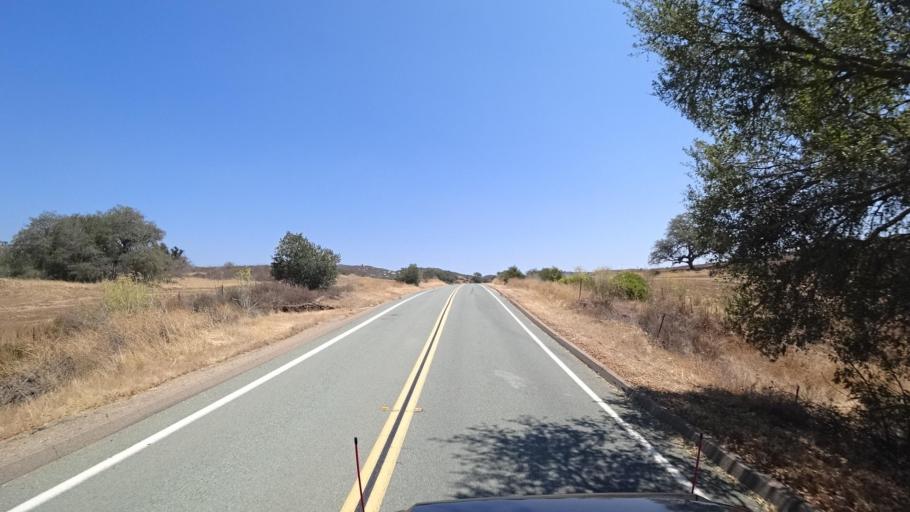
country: US
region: California
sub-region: San Diego County
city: Fallbrook
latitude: 33.4096
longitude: -117.2973
